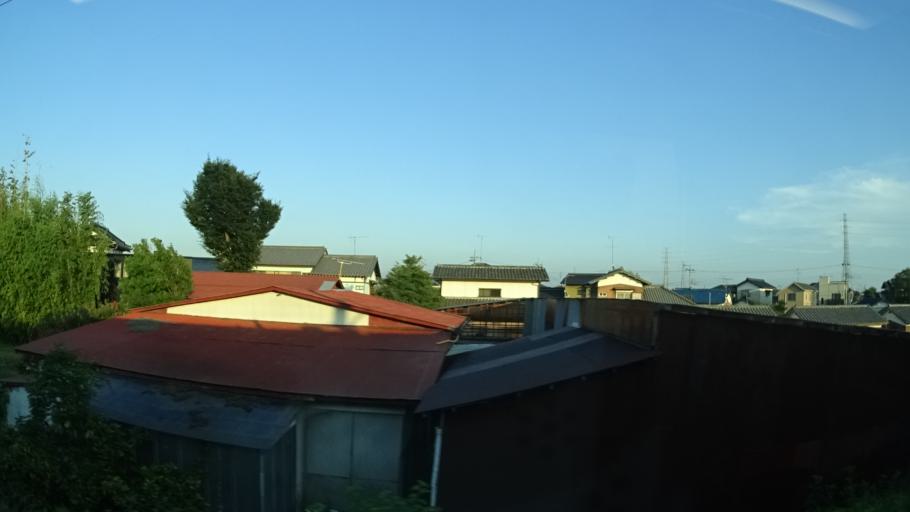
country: JP
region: Ibaraki
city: Fujishiro
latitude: 35.9261
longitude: 140.1355
